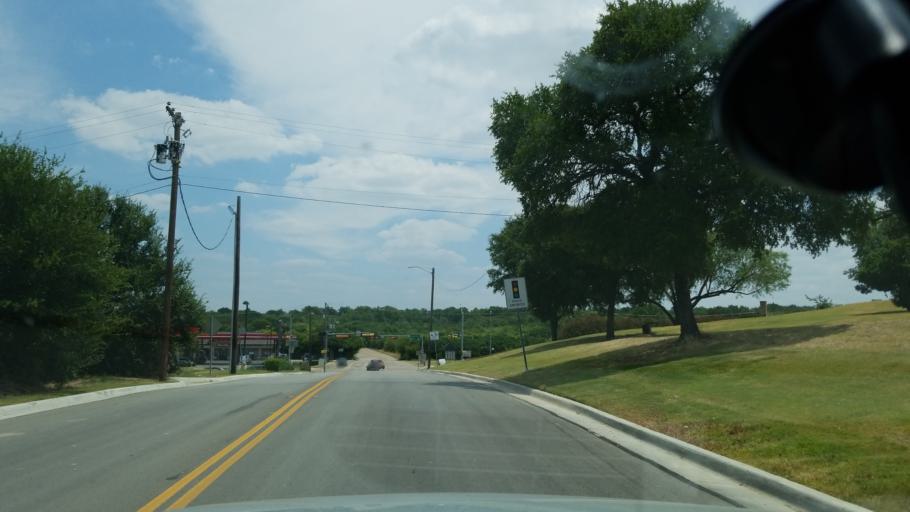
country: US
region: Texas
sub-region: Dallas County
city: Grand Prairie
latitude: 32.7550
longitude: -96.9963
